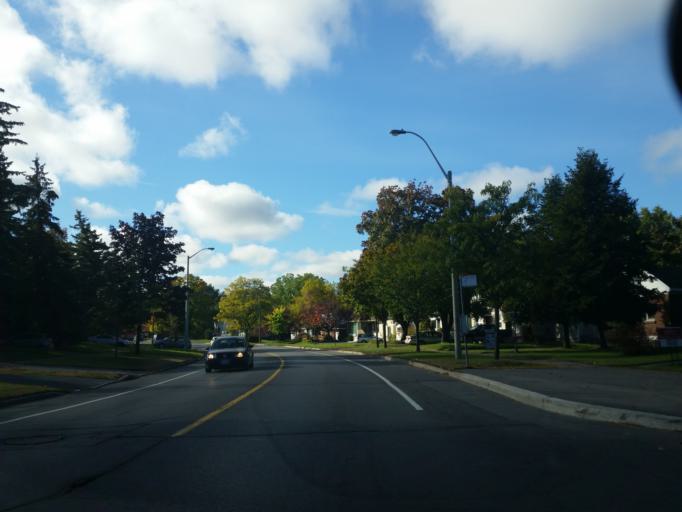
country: CA
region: Ontario
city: Ottawa
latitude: 45.3958
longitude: -75.6626
